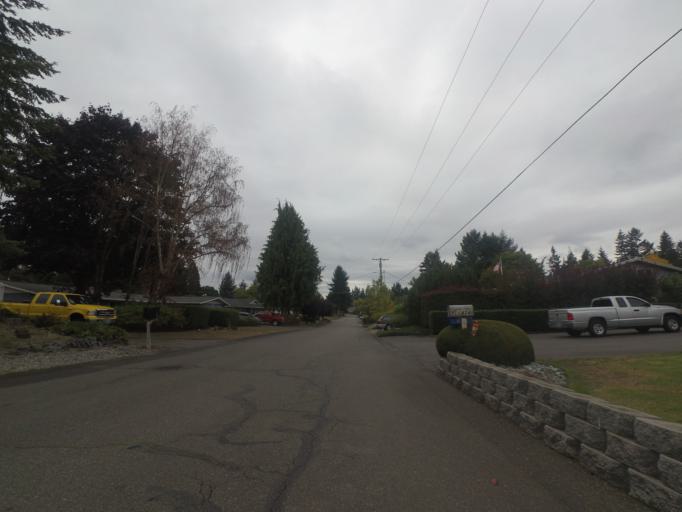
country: US
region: Washington
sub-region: Pierce County
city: Lakewood
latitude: 47.1533
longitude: -122.5131
